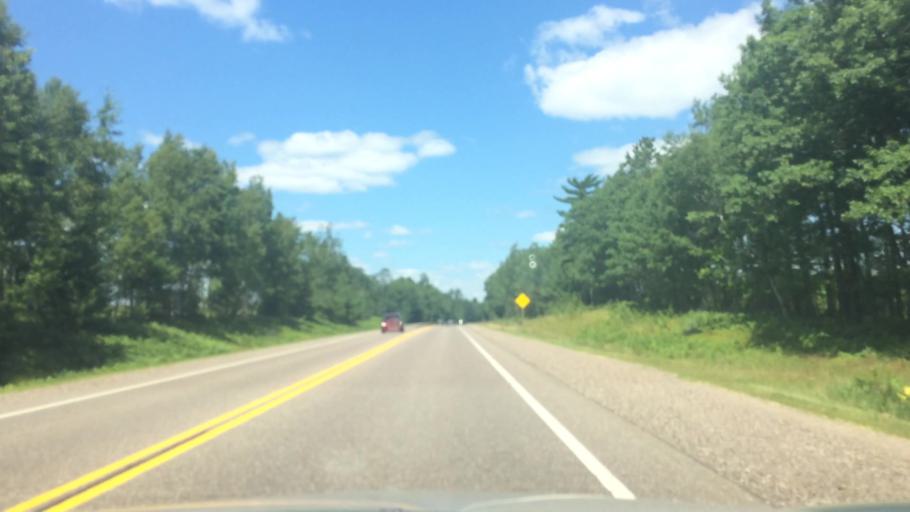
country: US
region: Wisconsin
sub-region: Vilas County
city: Lac du Flambeau
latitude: 45.9443
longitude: -89.6979
